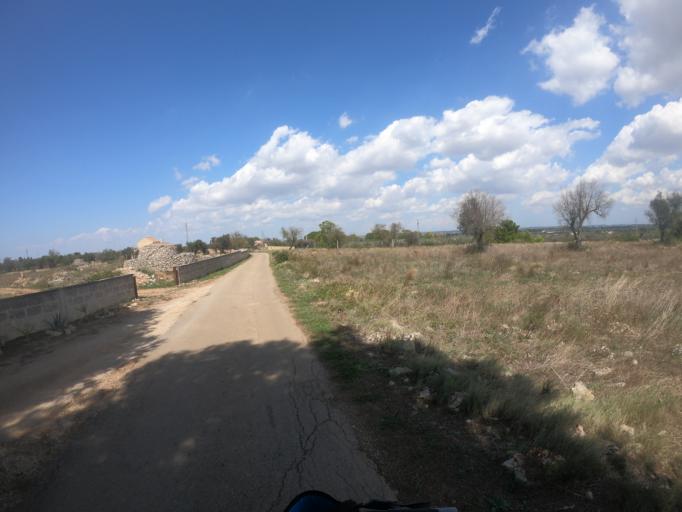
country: IT
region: Apulia
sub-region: Provincia di Lecce
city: Galatone
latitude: 40.1233
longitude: 18.0787
